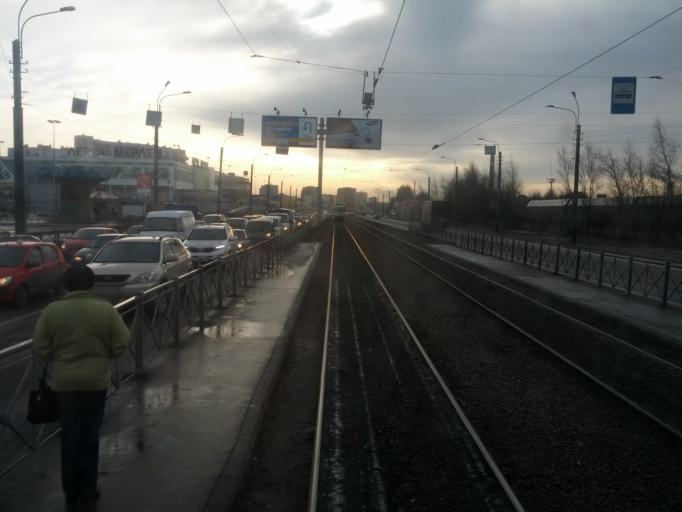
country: RU
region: St.-Petersburg
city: Obukhovo
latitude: 59.9121
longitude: 30.4399
